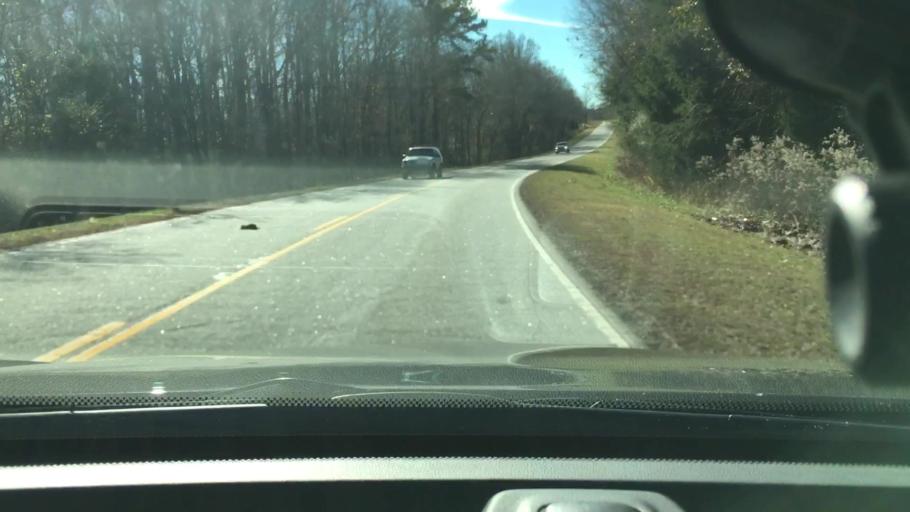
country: US
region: South Carolina
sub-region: Cherokee County
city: Gaffney
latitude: 35.0103
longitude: -81.6877
